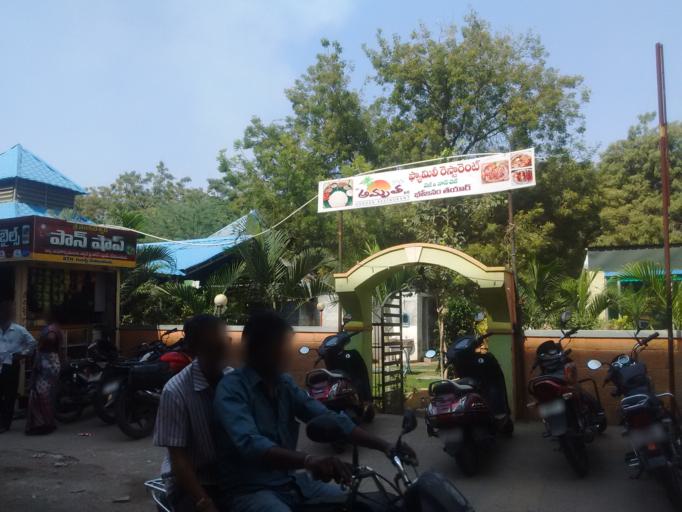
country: IN
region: Telangana
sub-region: Mahbubnagar
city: Alampur
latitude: 15.8133
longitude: 78.0400
